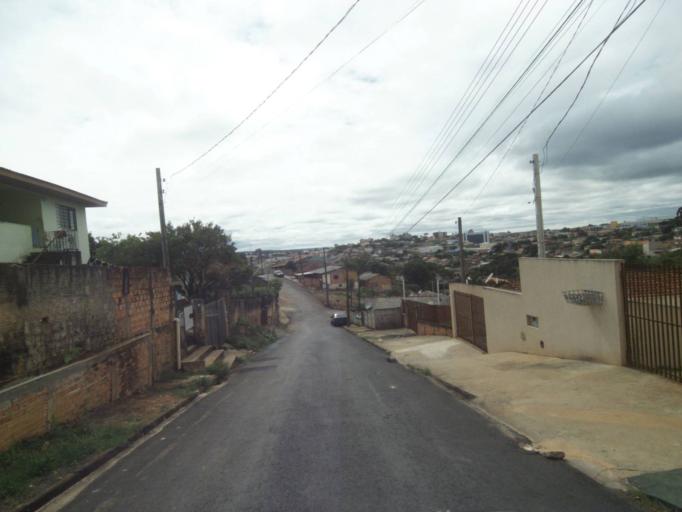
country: BR
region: Parana
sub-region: Telemaco Borba
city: Telemaco Borba
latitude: -24.3309
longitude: -50.6434
